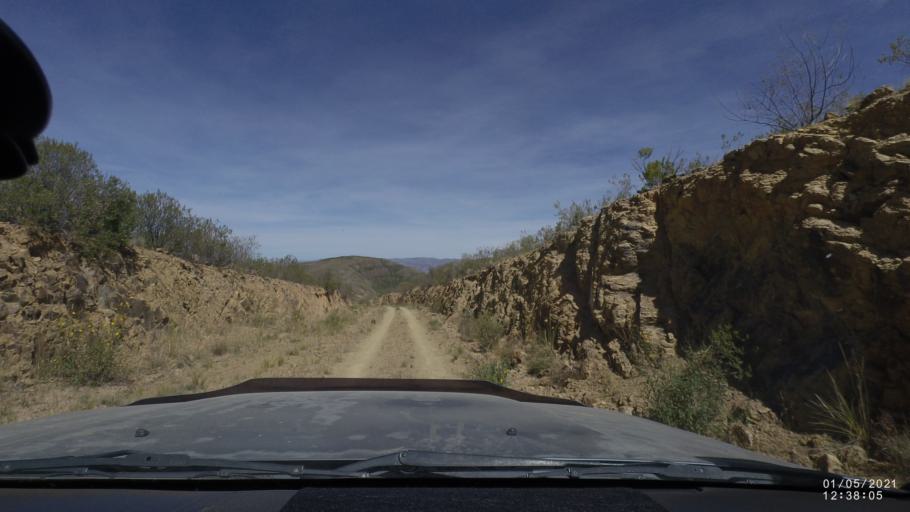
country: BO
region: Cochabamba
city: Capinota
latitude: -17.6795
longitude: -66.1583
